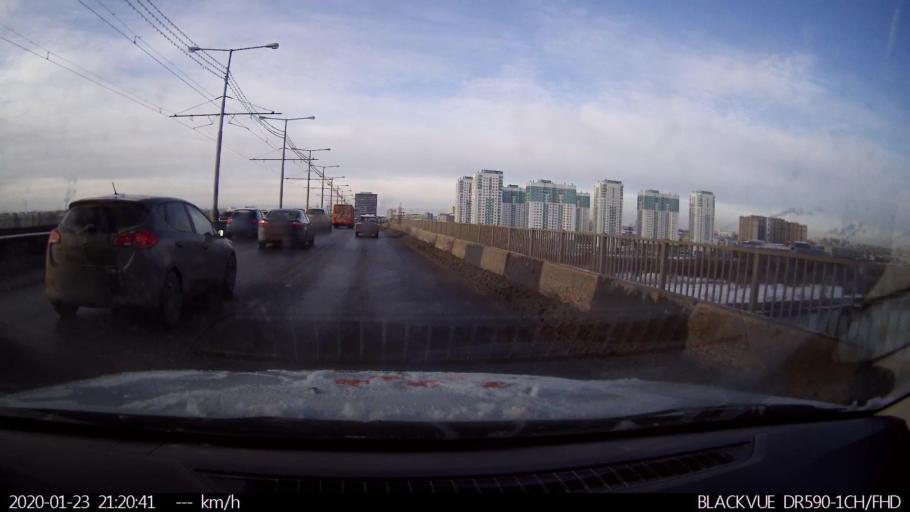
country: RU
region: Nizjnij Novgorod
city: Nizhniy Novgorod
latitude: 56.2976
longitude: 43.9614
